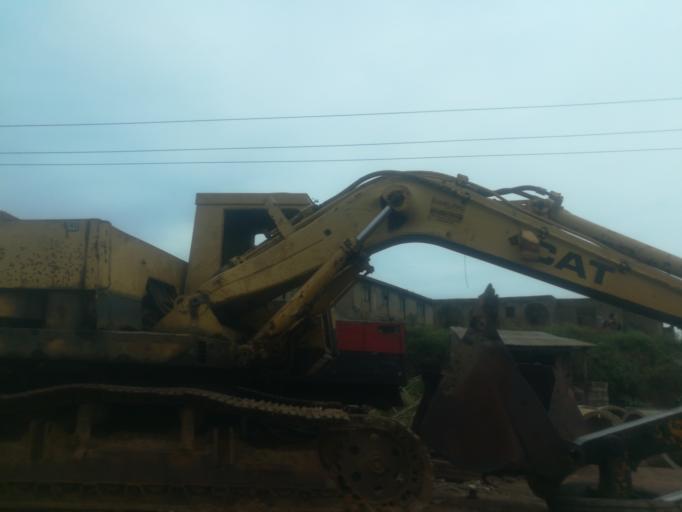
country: NG
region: Oyo
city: Ibadan
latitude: 7.3741
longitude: 3.9299
